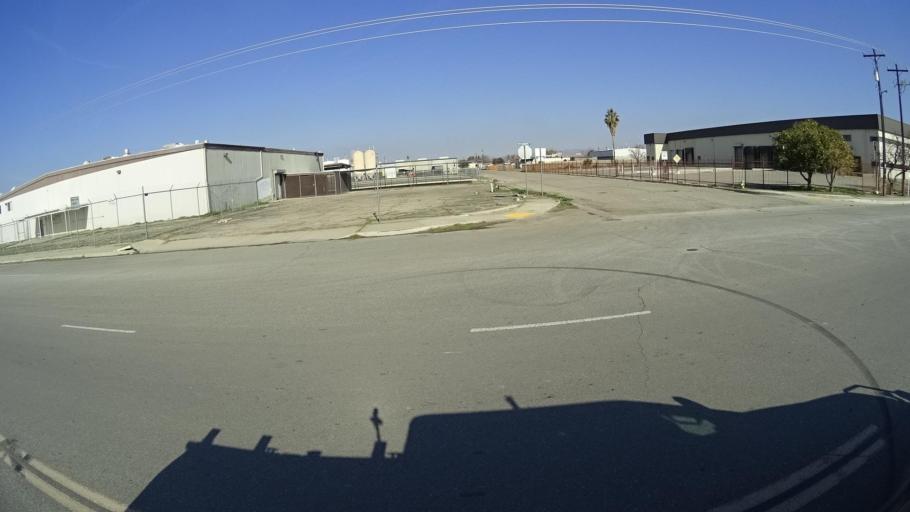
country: US
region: California
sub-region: Kern County
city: Arvin
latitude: 35.1945
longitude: -118.8254
